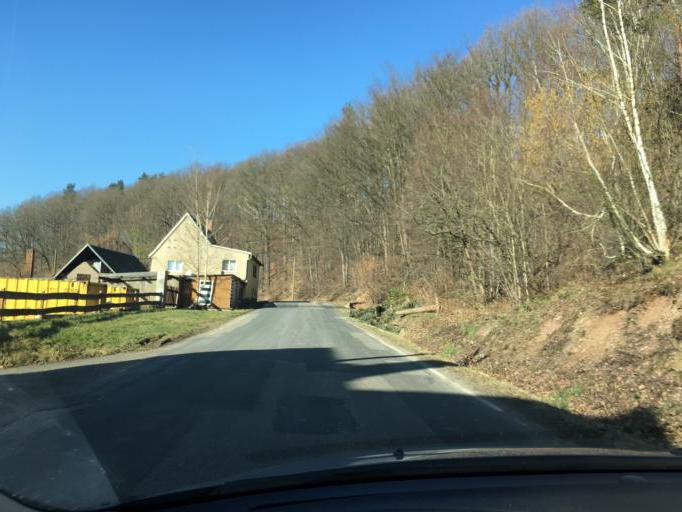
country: DE
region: Saxony
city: Lunzenau
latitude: 50.9683
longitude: 12.7232
